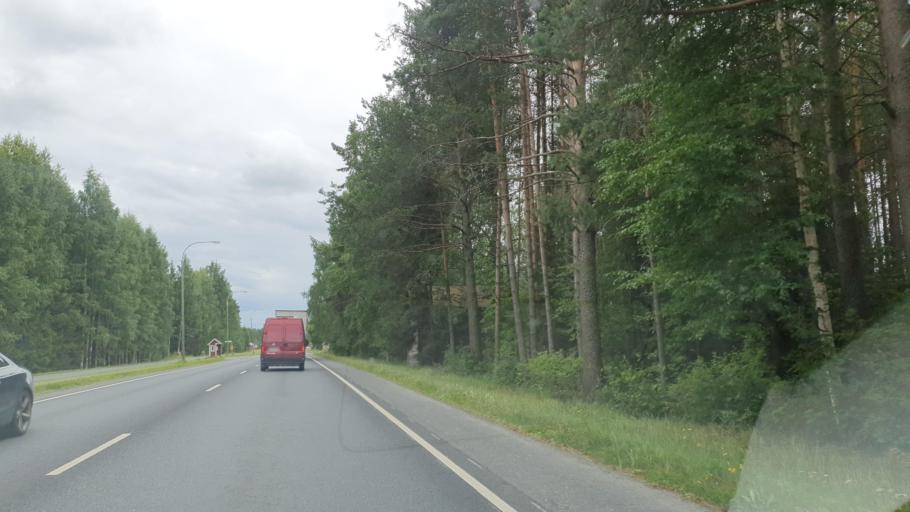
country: FI
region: Northern Savo
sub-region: Ylae-Savo
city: Lapinlahti
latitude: 63.4666
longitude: 27.3071
